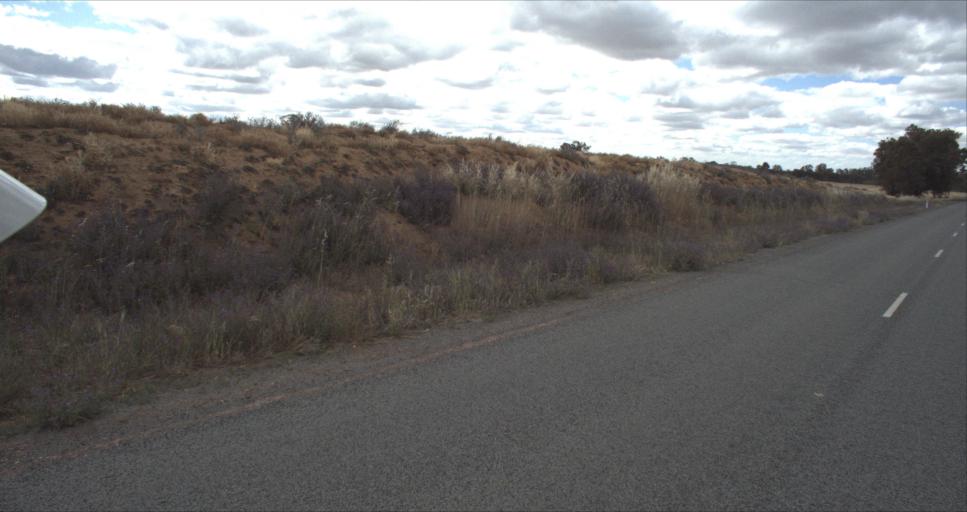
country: AU
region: New South Wales
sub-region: Leeton
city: Leeton
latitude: -34.6734
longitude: 146.3470
